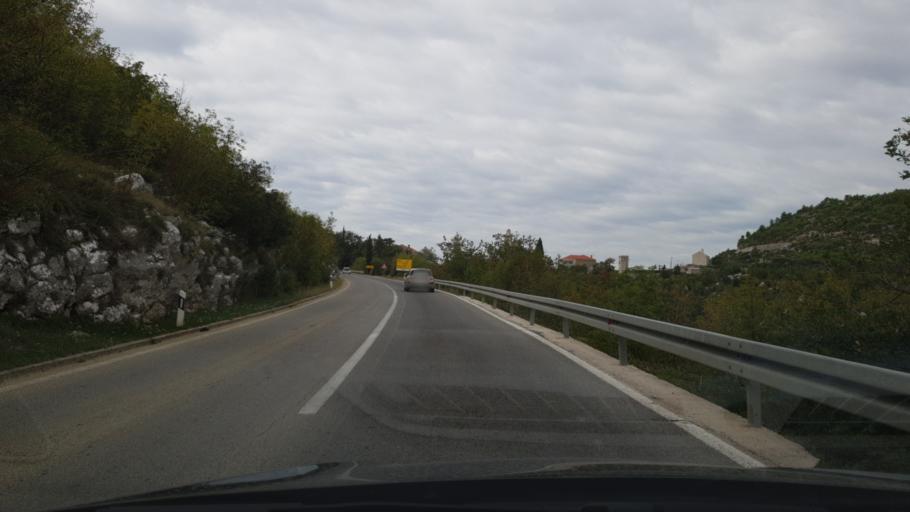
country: HR
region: Dubrovacko-Neretvanska
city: Cibaca
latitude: 42.6429
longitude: 18.1617
